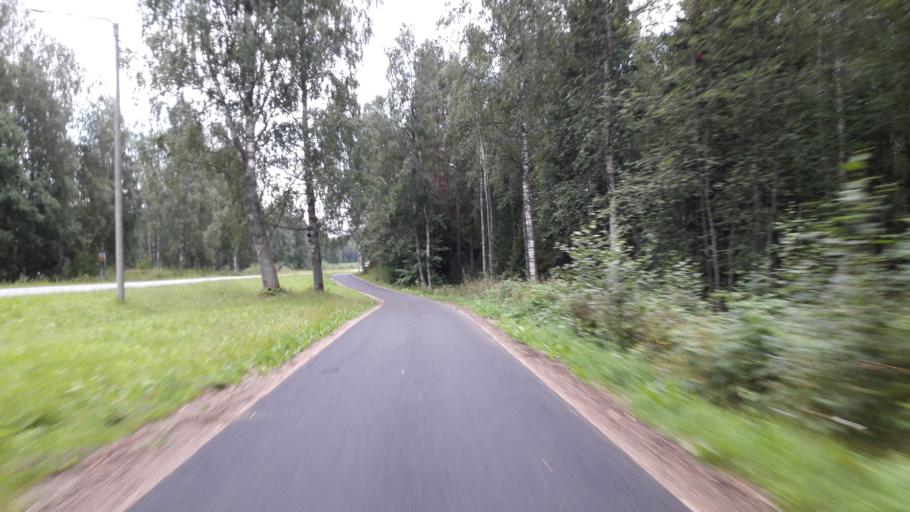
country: FI
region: North Karelia
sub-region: Joensuu
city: Joensuu
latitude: 62.5346
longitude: 29.8485
